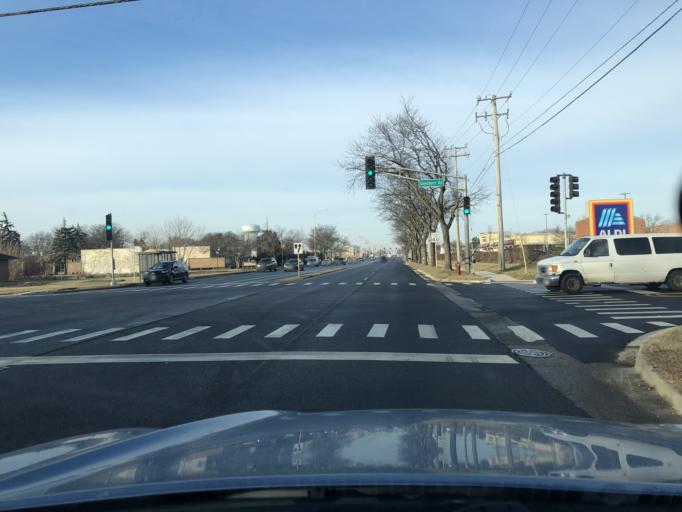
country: US
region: Illinois
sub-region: Cook County
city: Arlington Heights
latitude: 42.0515
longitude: -87.9746
